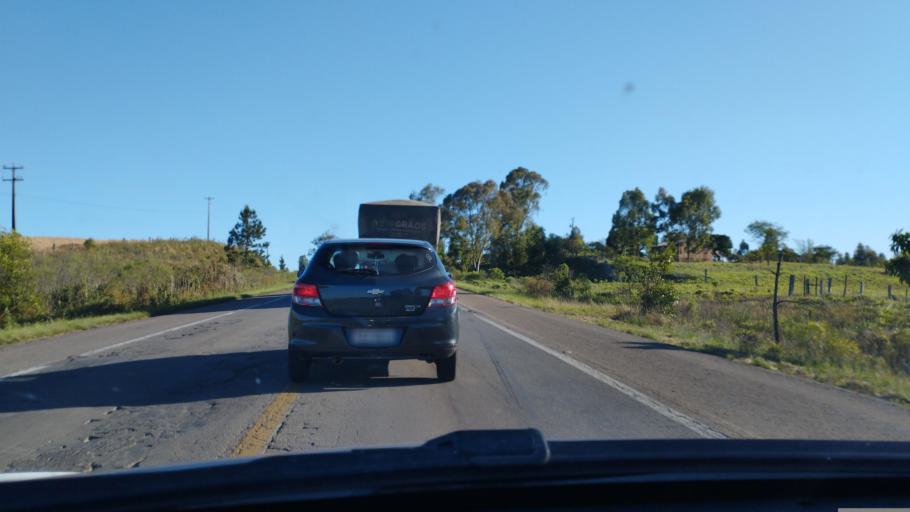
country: BR
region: Rio Grande do Sul
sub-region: Julio De Castilhos
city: Julio de Castilhos
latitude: -29.3753
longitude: -53.6708
